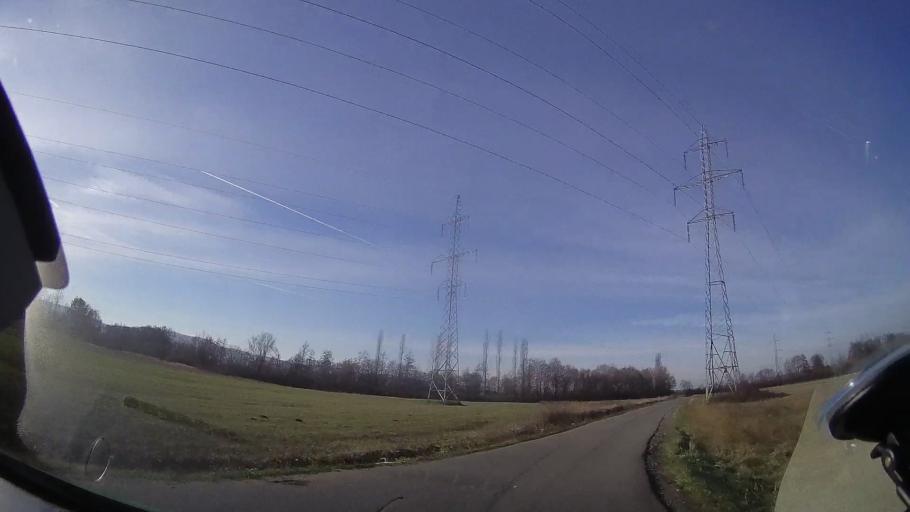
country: RO
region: Bihor
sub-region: Comuna Auseu
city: Grosi
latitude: 47.0269
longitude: 22.4812
